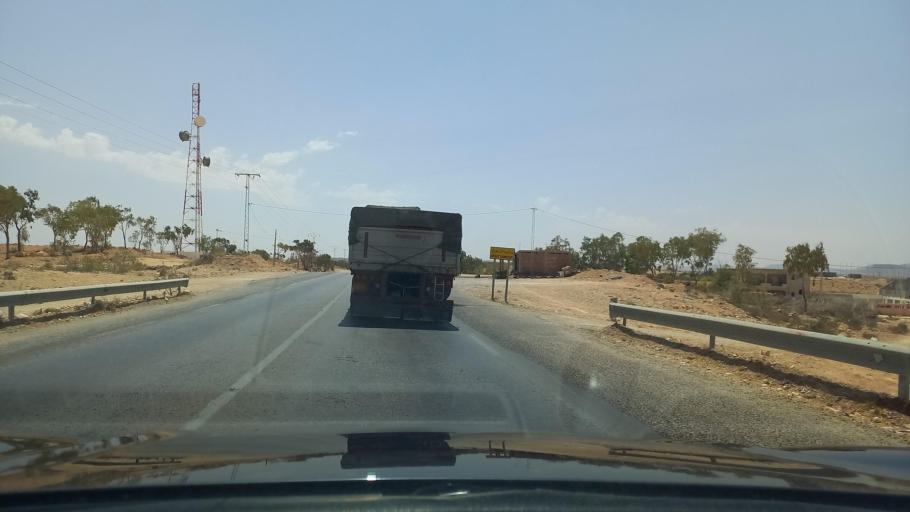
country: TN
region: Madanin
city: Medenine
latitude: 33.5702
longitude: 10.3171
